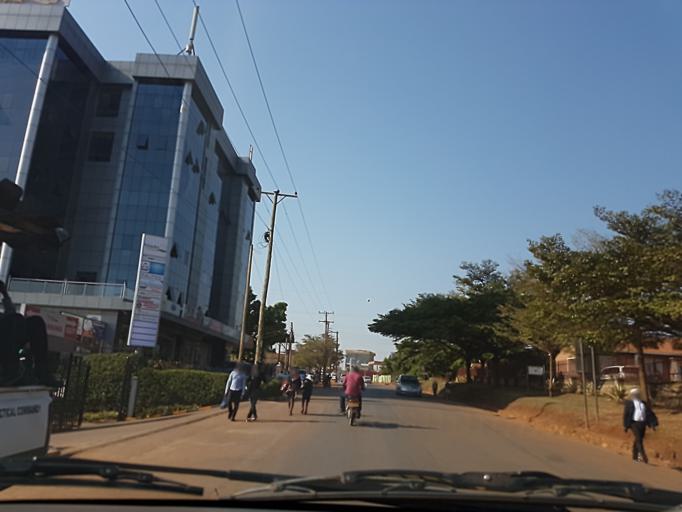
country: UG
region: Central Region
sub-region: Wakiso District
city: Kireka
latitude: 0.3528
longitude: 32.6151
